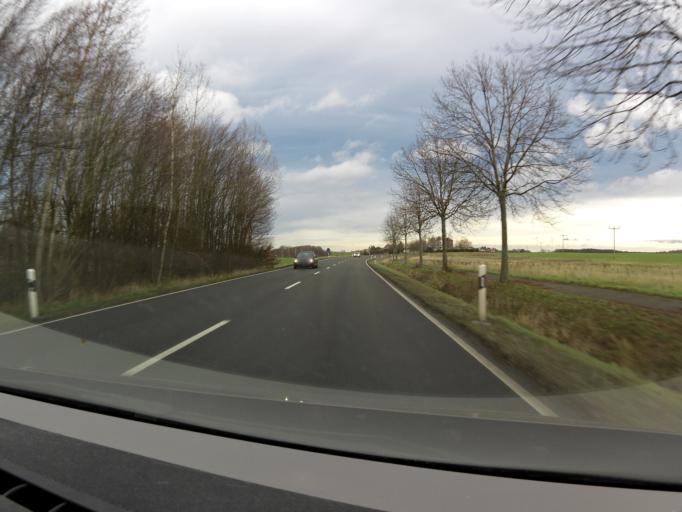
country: DE
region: Saxony-Anhalt
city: Blankenheim
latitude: 51.5540
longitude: 11.4081
